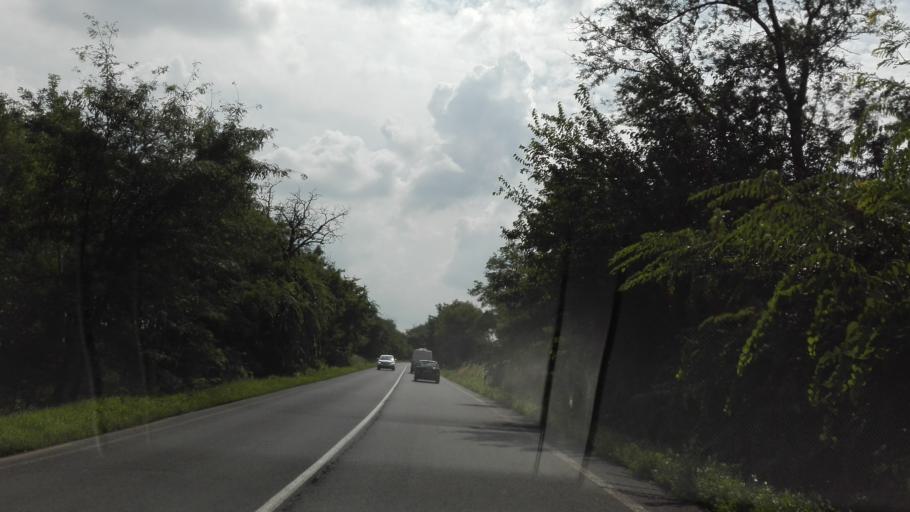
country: HU
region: Fejer
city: Alap
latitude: 46.7776
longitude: 18.6691
